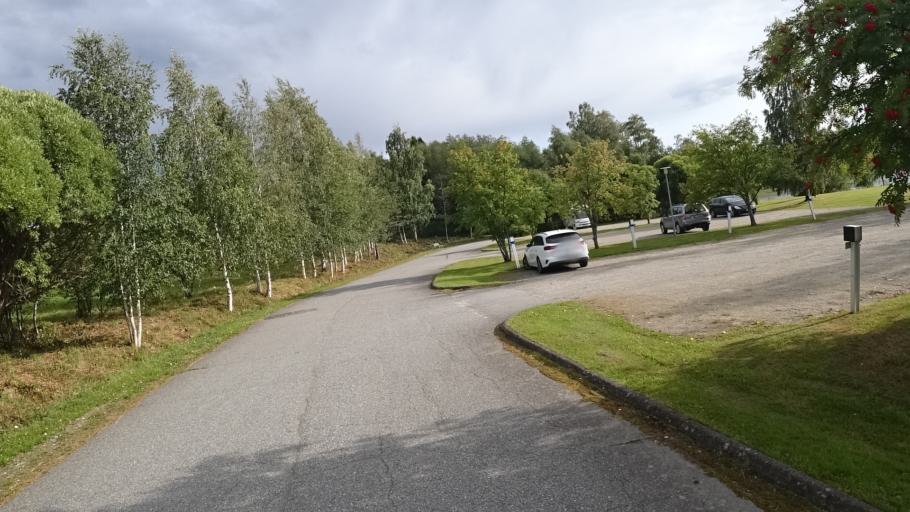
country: FI
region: North Karelia
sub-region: Joensuu
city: Ilomantsi
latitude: 62.6746
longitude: 30.9133
